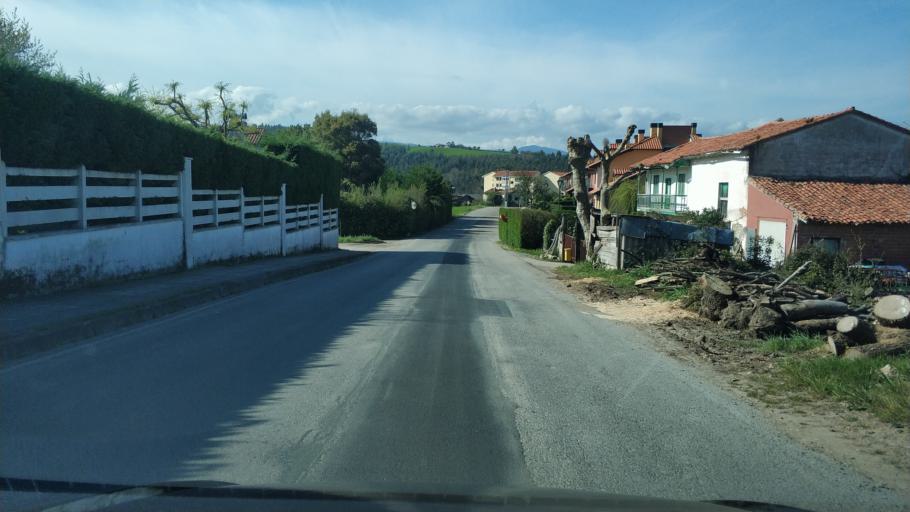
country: ES
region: Cantabria
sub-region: Provincia de Cantabria
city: Comillas
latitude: 43.3789
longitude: -4.2829
